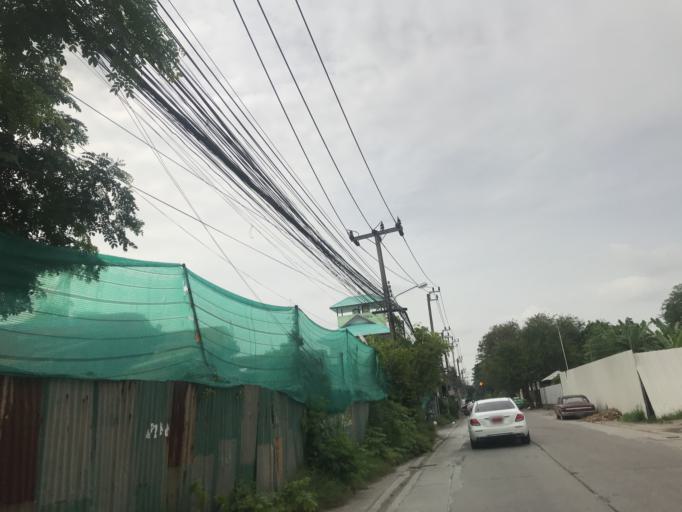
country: TH
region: Bangkok
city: Bang Kapi
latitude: 13.7496
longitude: 100.6347
